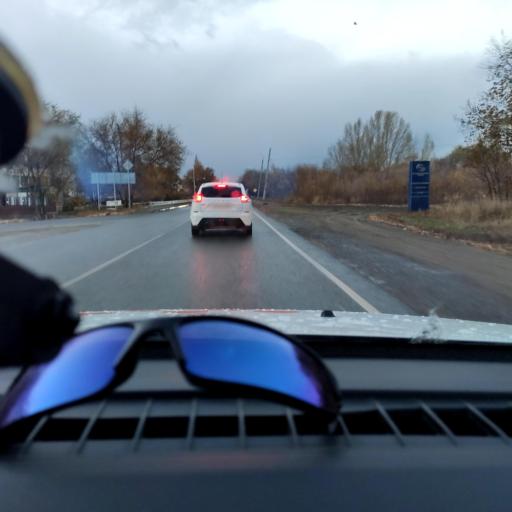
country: RU
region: Samara
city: Samara
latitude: 53.1308
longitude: 50.1082
